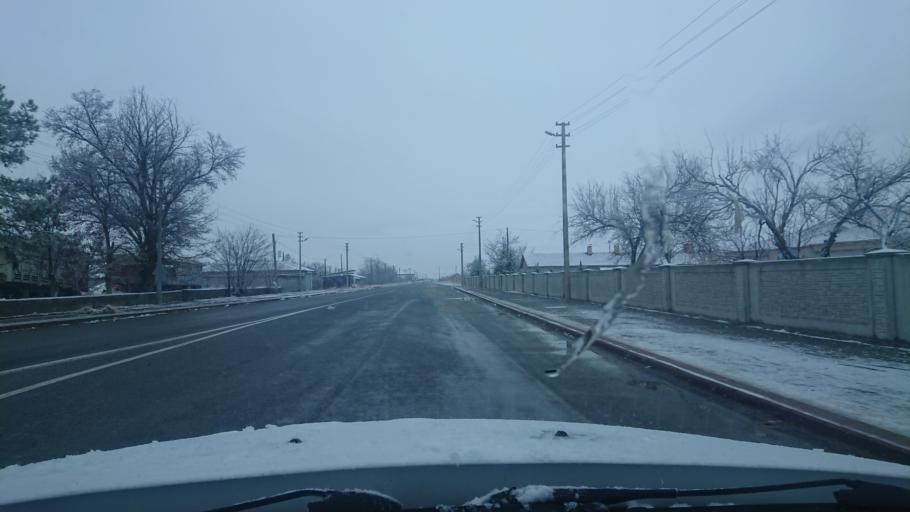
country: TR
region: Aksaray
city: Yesilova
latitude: 38.2916
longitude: 33.7604
